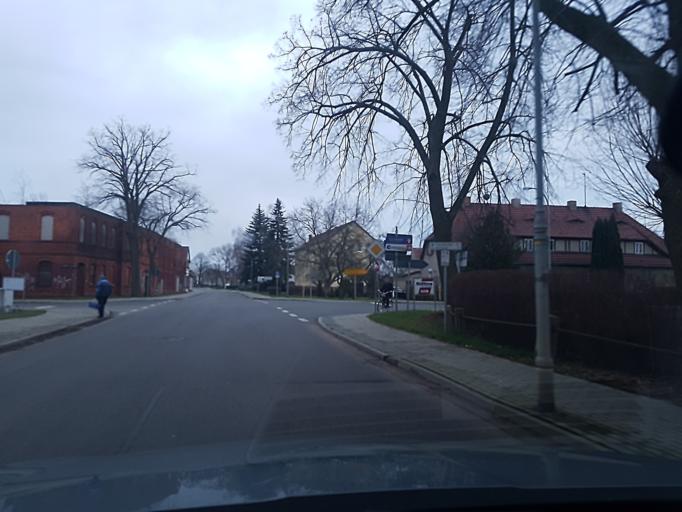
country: DE
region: Brandenburg
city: Sonnewalde
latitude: 51.6939
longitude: 13.6457
